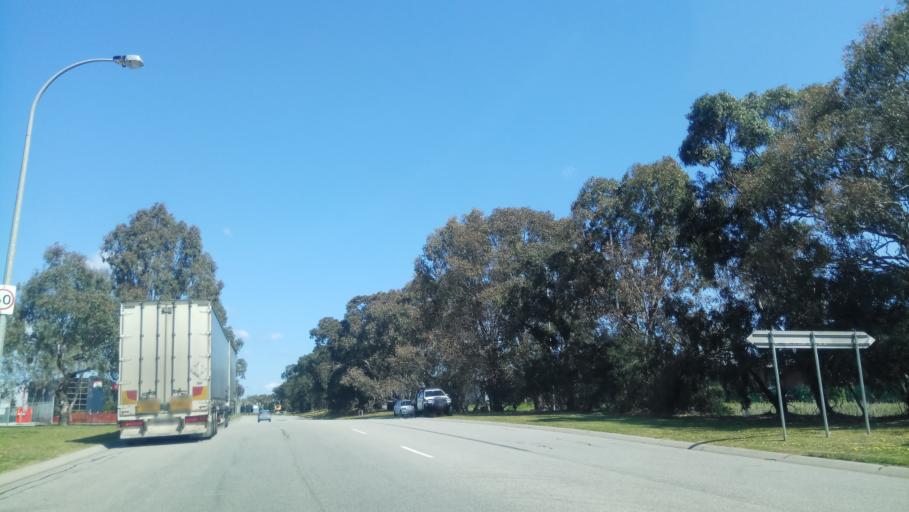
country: AU
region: Victoria
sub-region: Kingston
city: Dingley Village
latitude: -37.9884
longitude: 145.1177
